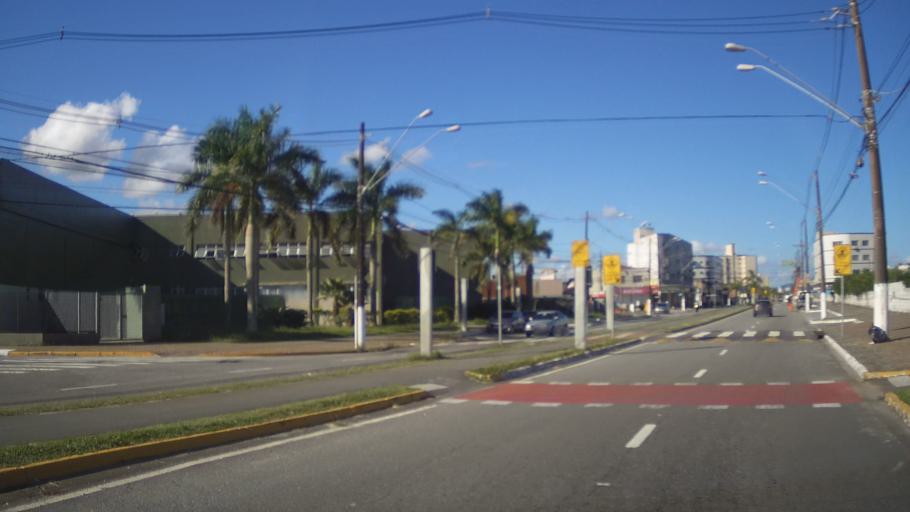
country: BR
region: Sao Paulo
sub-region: Praia Grande
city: Praia Grande
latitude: -24.0309
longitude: -46.4928
